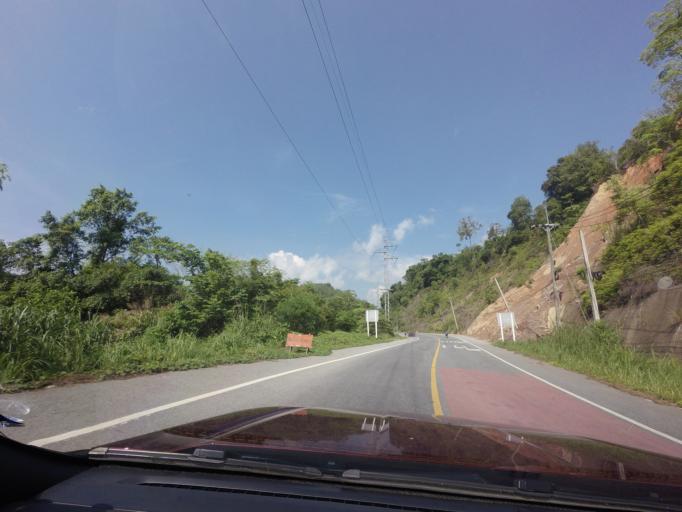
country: TH
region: Yala
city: Than To
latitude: 5.9595
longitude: 101.1939
